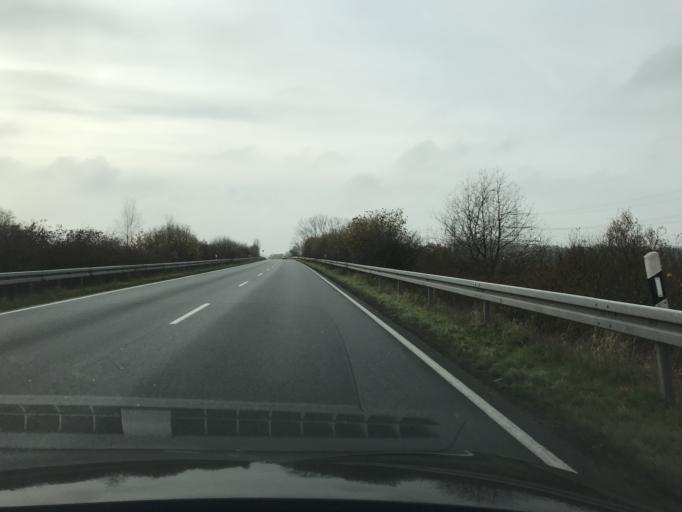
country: DE
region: North Rhine-Westphalia
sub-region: Regierungsbezirk Arnsberg
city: Hamm
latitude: 51.7168
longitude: 7.7591
